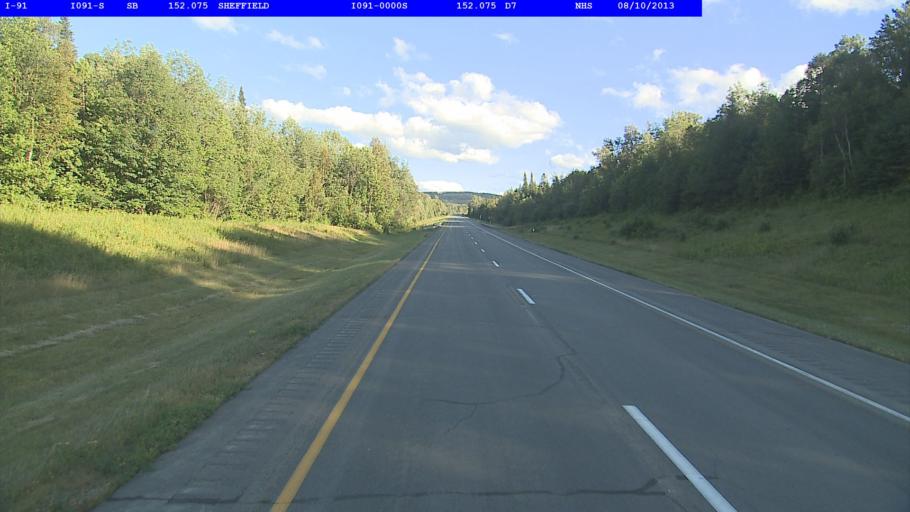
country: US
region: Vermont
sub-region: Caledonia County
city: Lyndonville
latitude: 44.6937
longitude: -72.1406
